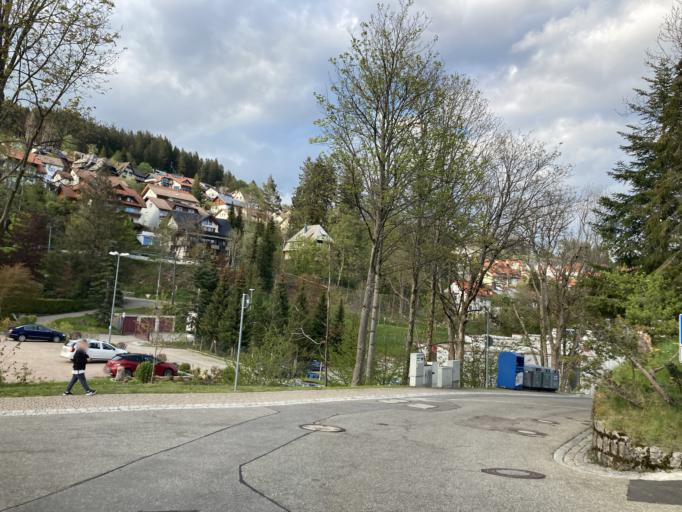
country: DE
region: Baden-Wuerttemberg
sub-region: Freiburg Region
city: Schonach im Schwarzwald
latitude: 48.1420
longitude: 8.2032
